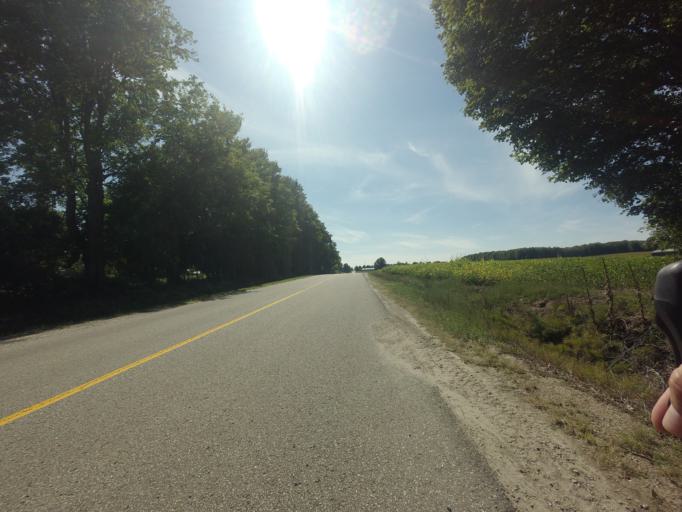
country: CA
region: Ontario
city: Perth
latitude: 44.9606
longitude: -76.2877
